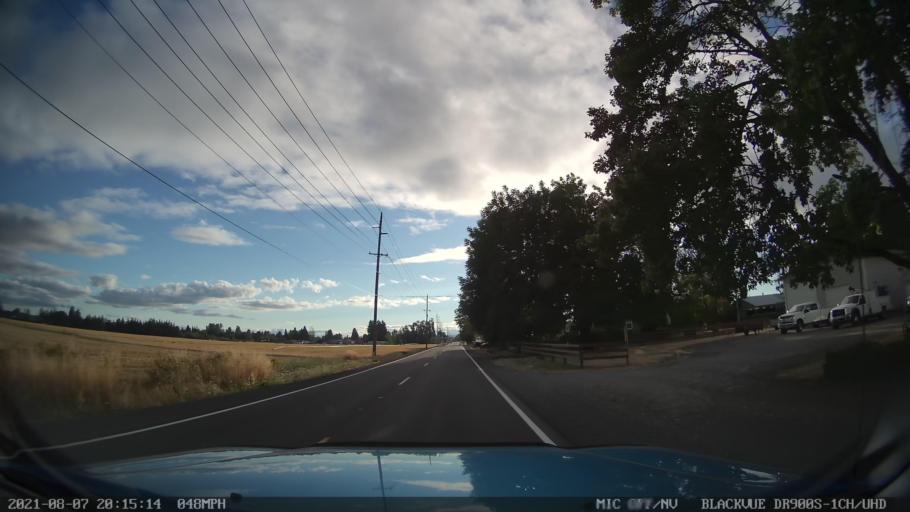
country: US
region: Oregon
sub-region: Marion County
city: Four Corners
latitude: 44.9549
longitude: -122.9527
